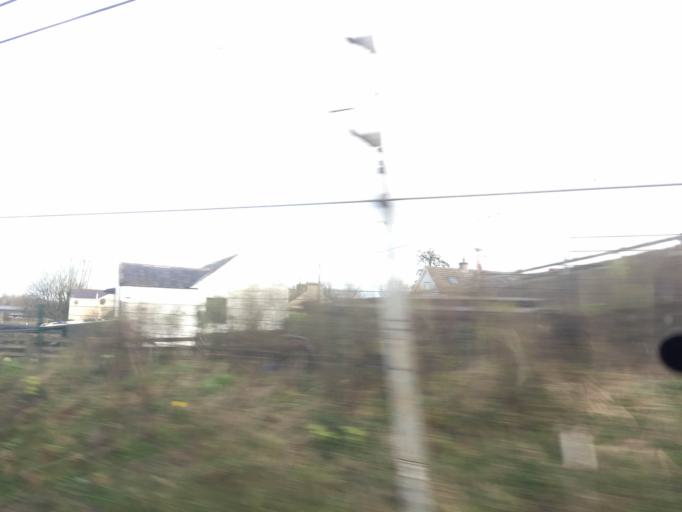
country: GB
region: England
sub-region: Cumbria
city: Penrith
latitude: 54.6342
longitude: -2.7251
